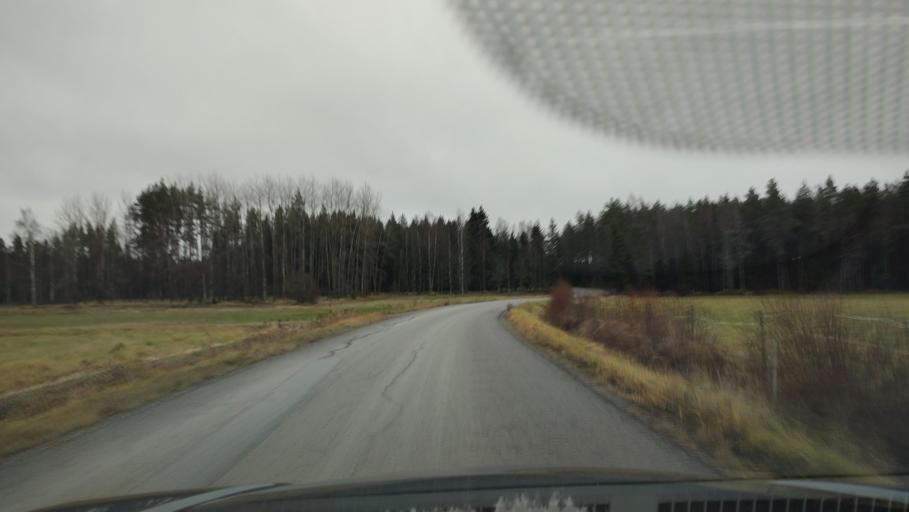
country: FI
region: Southern Ostrobothnia
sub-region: Suupohja
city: Karijoki
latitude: 62.1271
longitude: 21.5916
